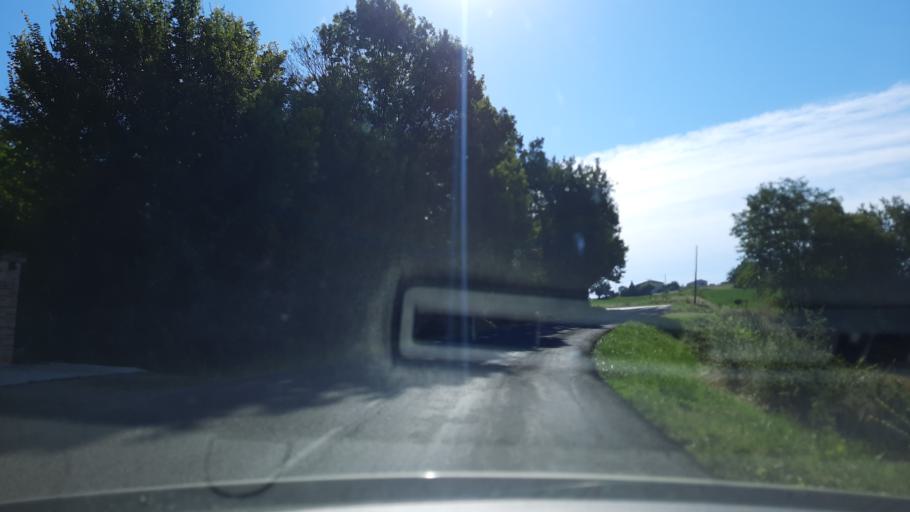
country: FR
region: Midi-Pyrenees
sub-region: Departement du Tarn-et-Garonne
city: Molieres
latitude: 44.1855
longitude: 1.3500
